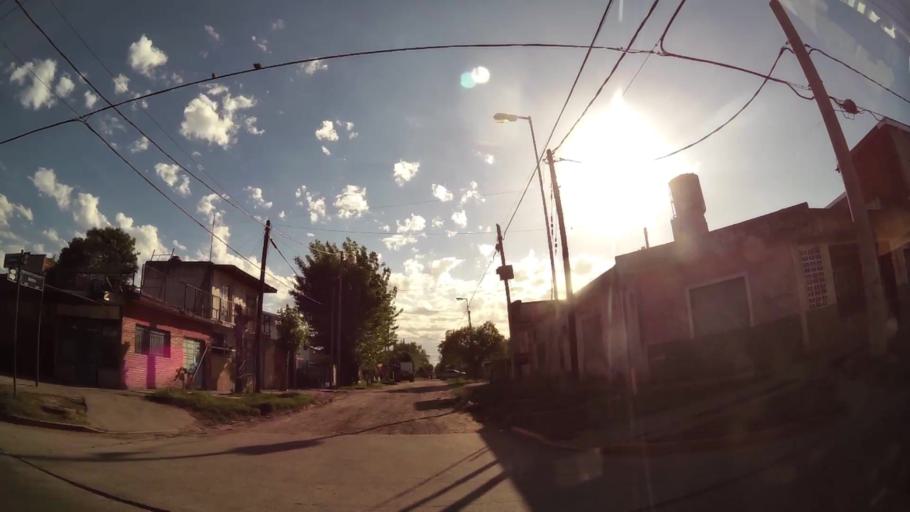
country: AR
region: Buenos Aires
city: Santa Catalina - Dique Lujan
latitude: -34.4925
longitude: -58.7218
